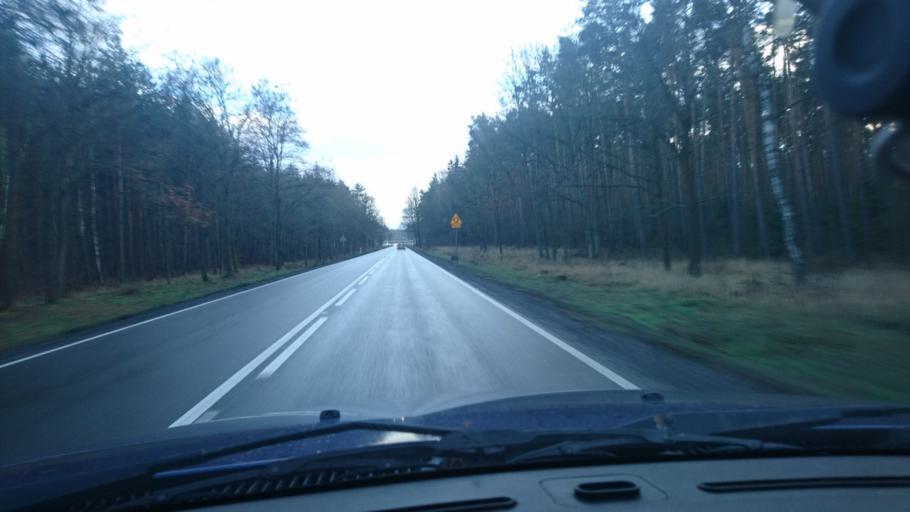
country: PL
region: Greater Poland Voivodeship
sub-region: Powiat kepinski
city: Kepno
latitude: 51.3359
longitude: 17.9549
